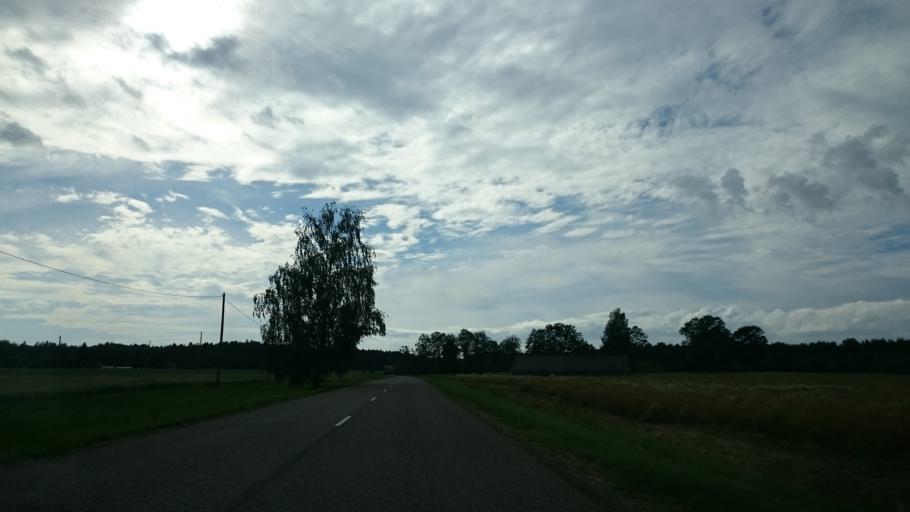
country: LV
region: Saulkrastu
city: Saulkrasti
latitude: 57.2499
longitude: 24.5108
